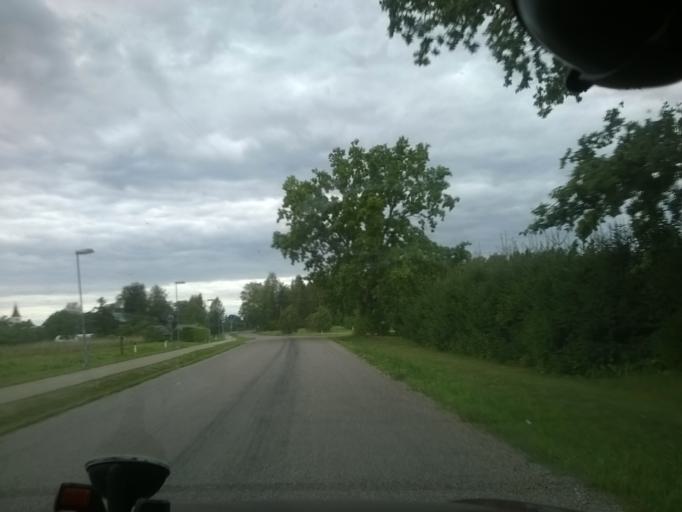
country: EE
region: Vorumaa
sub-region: Voru linn
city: Voru
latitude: 57.7297
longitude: 26.9375
